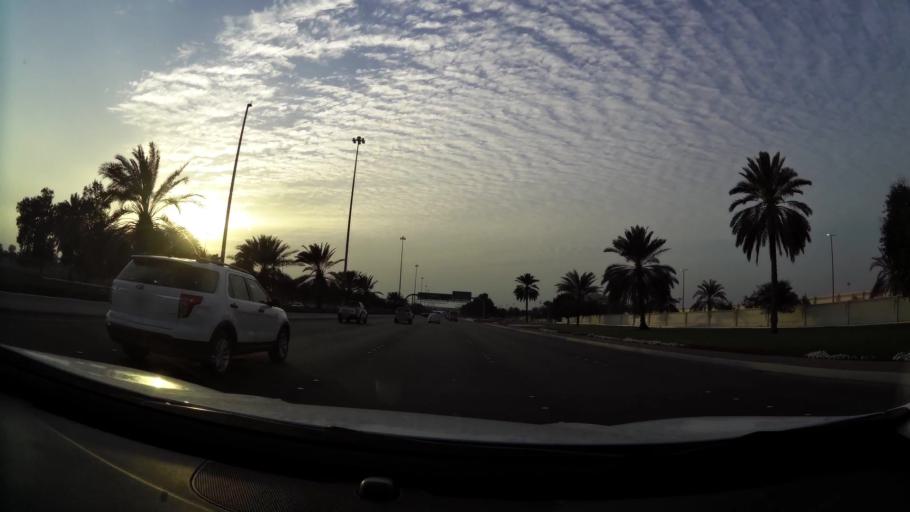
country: AE
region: Abu Dhabi
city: Abu Dhabi
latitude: 24.4211
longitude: 54.4228
